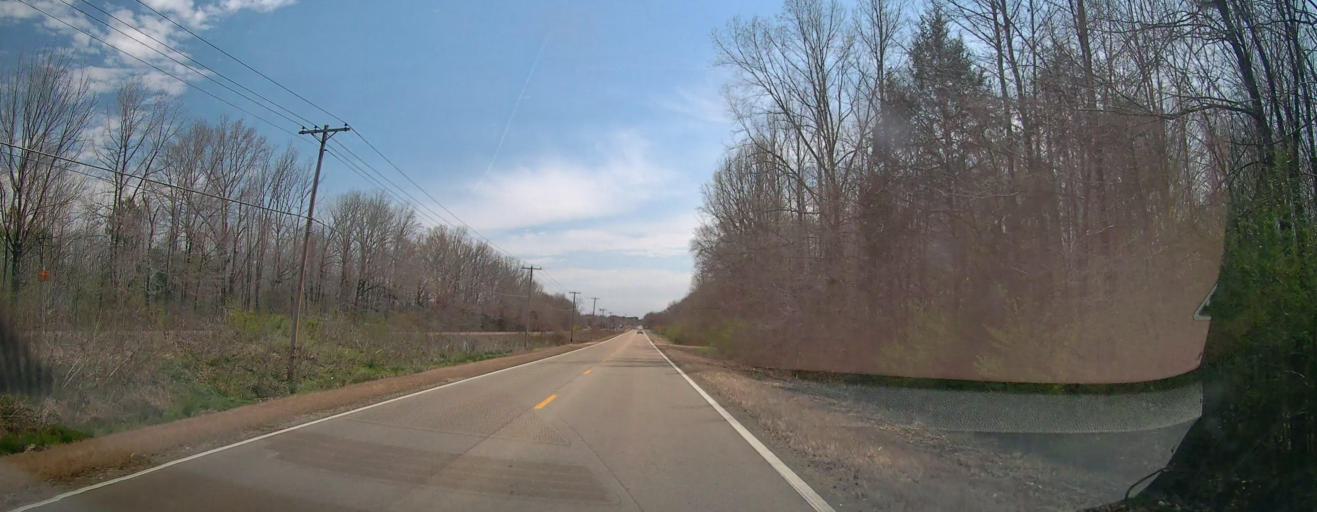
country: US
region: Mississippi
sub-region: Union County
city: New Albany
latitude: 34.5247
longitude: -89.0637
